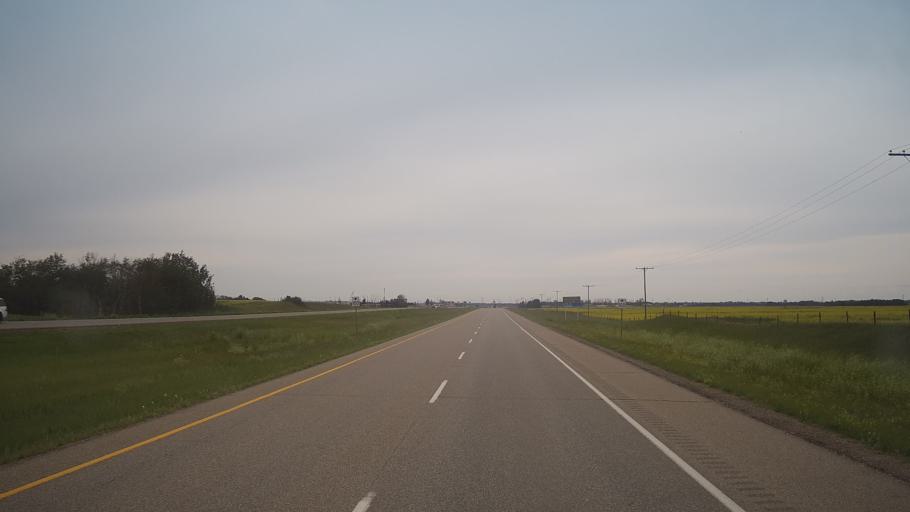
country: CA
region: Saskatchewan
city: Saskatoon
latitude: 52.0416
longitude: -106.5901
